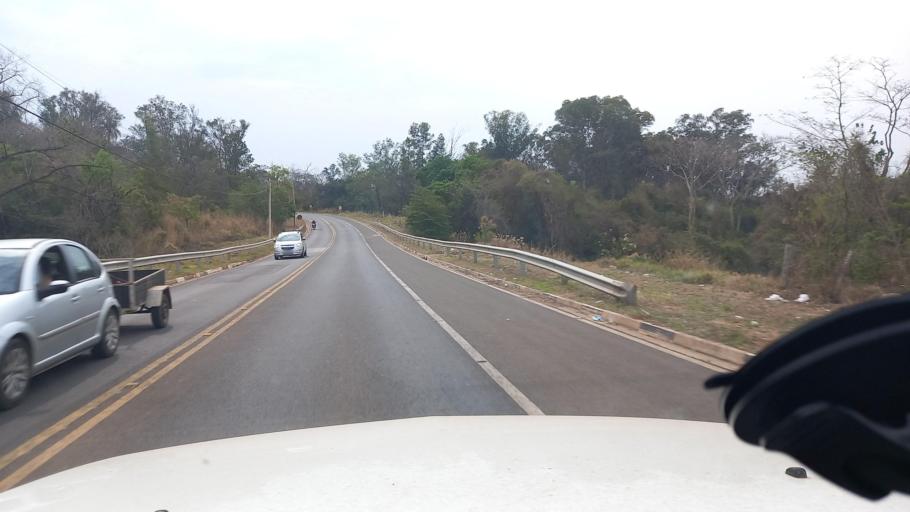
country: BR
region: Sao Paulo
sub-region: Moji-Guacu
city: Mogi-Gaucu
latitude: -22.3754
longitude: -46.9646
